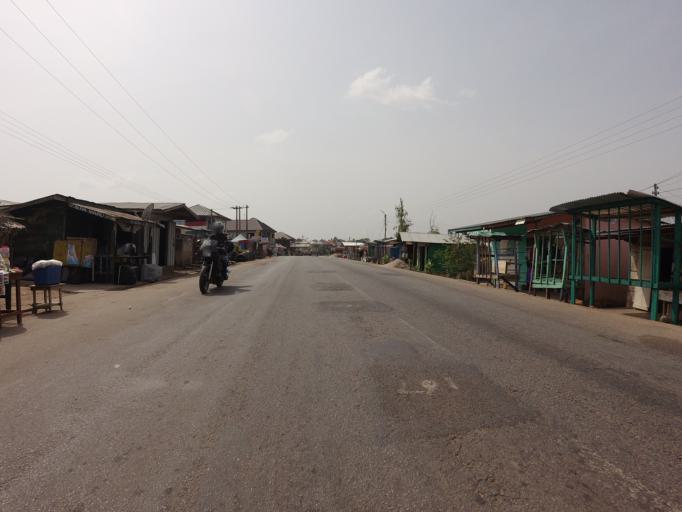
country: GH
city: Akropong
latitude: 6.2568
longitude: 0.1345
